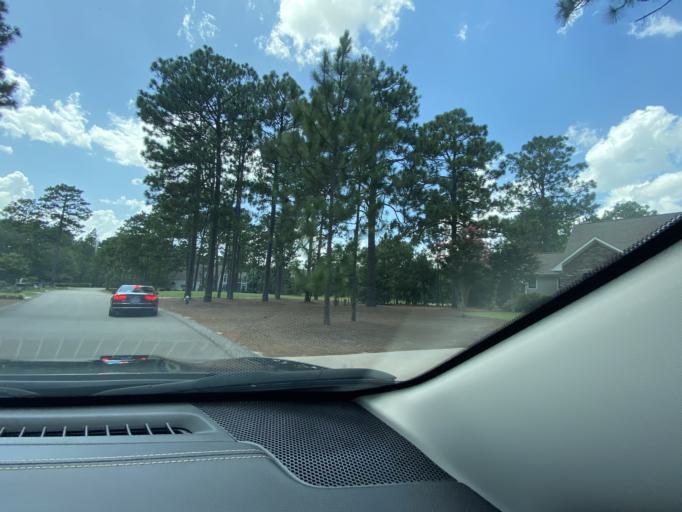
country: US
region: North Carolina
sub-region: Moore County
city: Pinehurst
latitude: 35.1874
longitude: -79.4362
